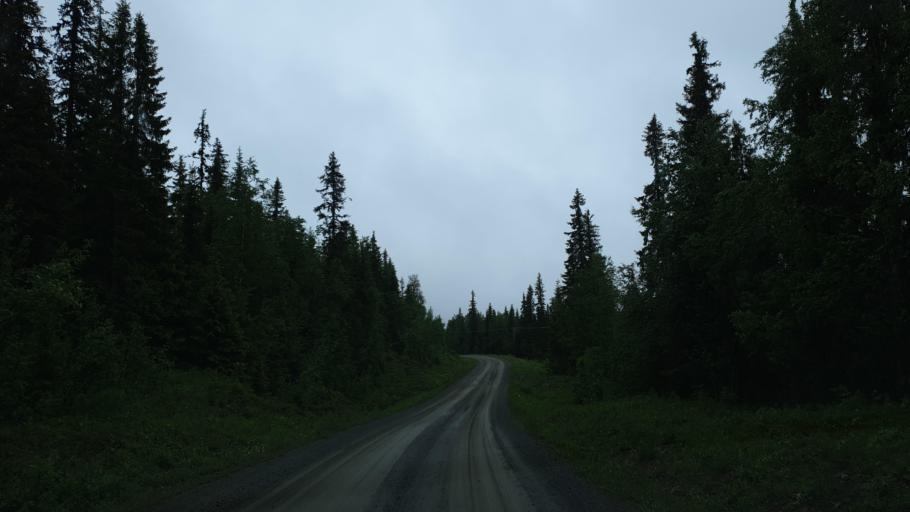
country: SE
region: Vaesterbotten
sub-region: Vilhelmina Kommun
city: Sjoberg
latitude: 65.3285
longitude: 15.9167
